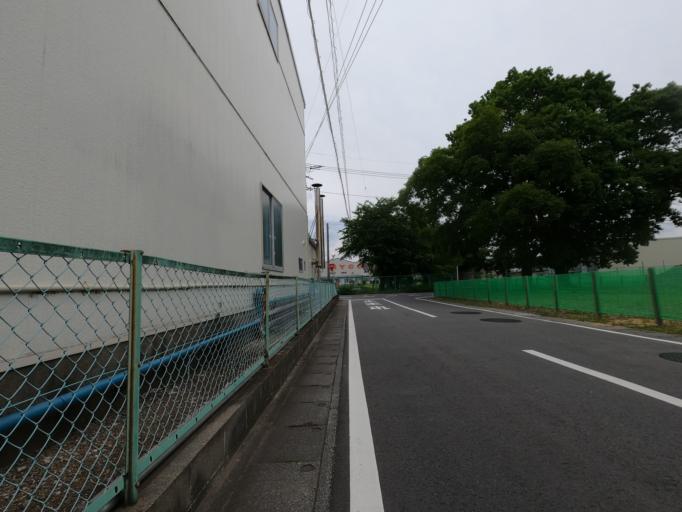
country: JP
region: Ibaraki
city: Moriya
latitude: 35.9582
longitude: 139.9827
